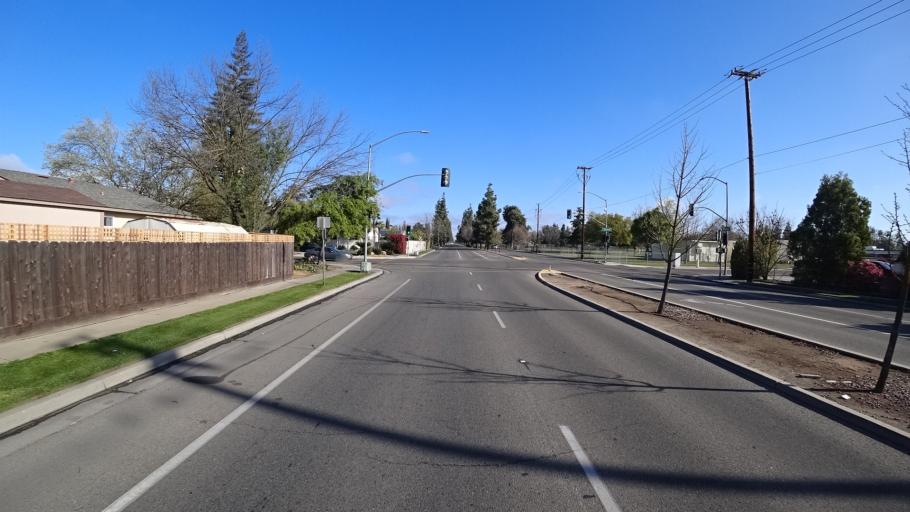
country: US
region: California
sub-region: Fresno County
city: Fresno
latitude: 36.8297
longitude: -119.8265
